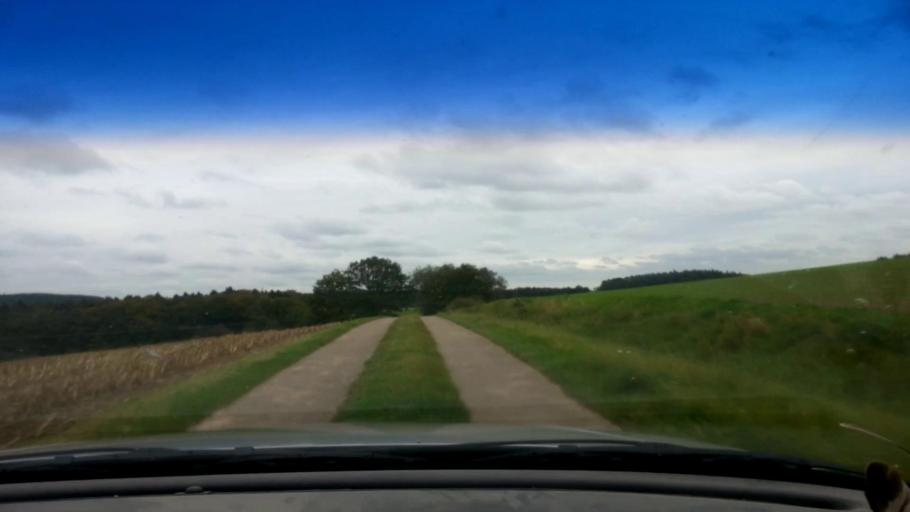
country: DE
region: Bavaria
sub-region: Regierungsbezirk Unterfranken
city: Kirchlauter
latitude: 50.0377
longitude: 10.7370
